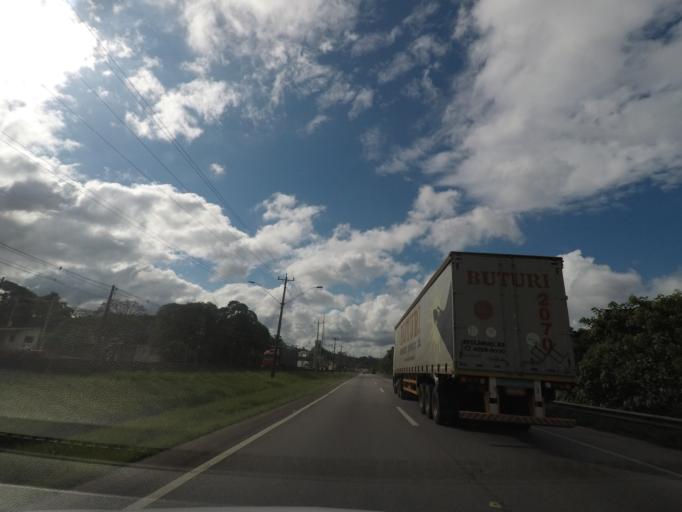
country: BR
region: Sao Paulo
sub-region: Itapecerica Da Serra
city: Itapecerica da Serra
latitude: -23.7512
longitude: -46.9011
